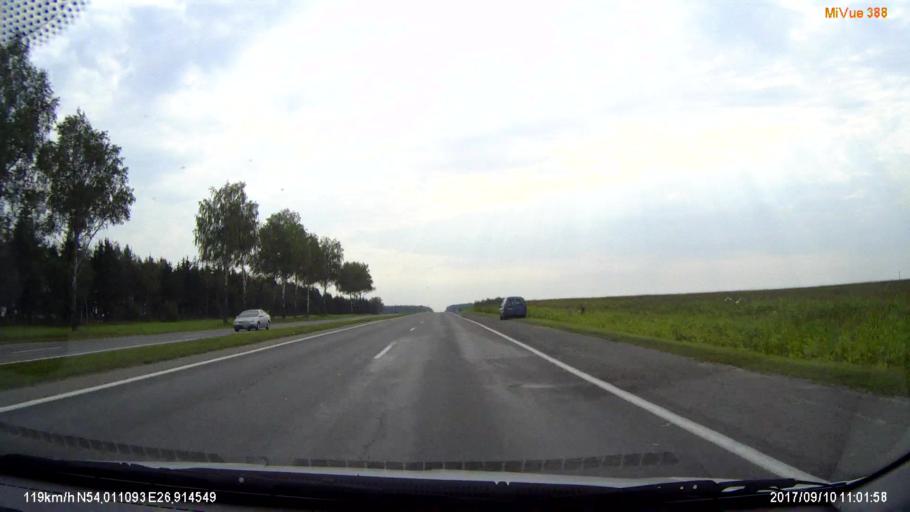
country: BY
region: Minsk
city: Rakaw
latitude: 54.0111
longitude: 26.9145
